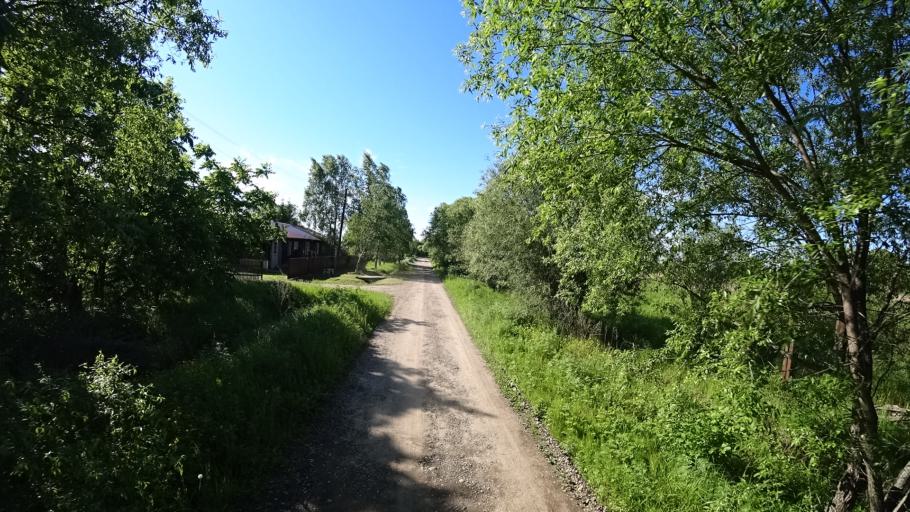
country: RU
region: Khabarovsk Krai
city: Khor
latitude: 47.8941
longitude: 134.9963
